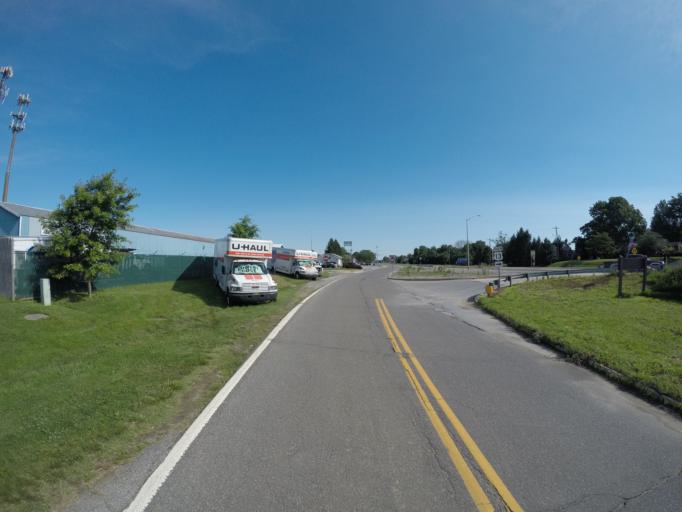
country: US
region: Delaware
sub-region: New Castle County
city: Delaware City
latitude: 39.5586
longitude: -75.6533
